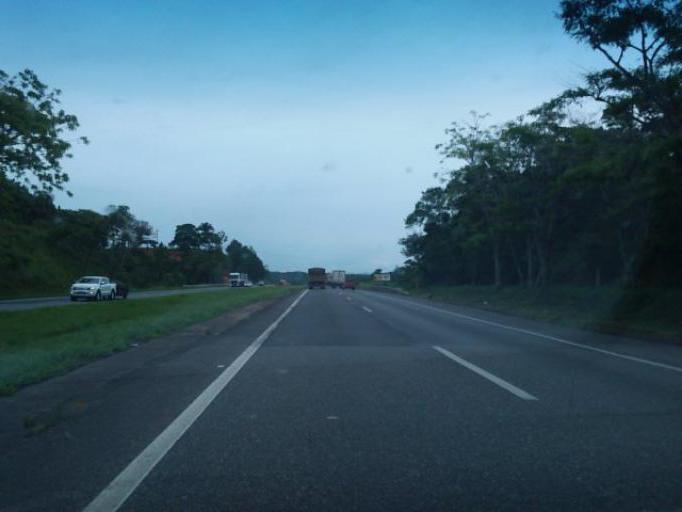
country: BR
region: Sao Paulo
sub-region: Pariquera-Acu
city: Pariquera Acu
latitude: -24.6386
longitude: -47.9127
